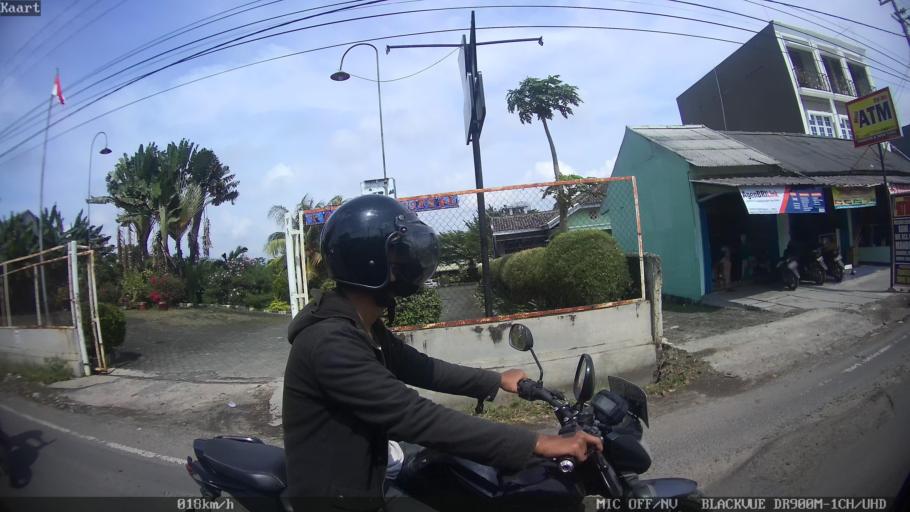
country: ID
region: Lampung
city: Kedaton
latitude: -5.3668
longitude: 105.2749
